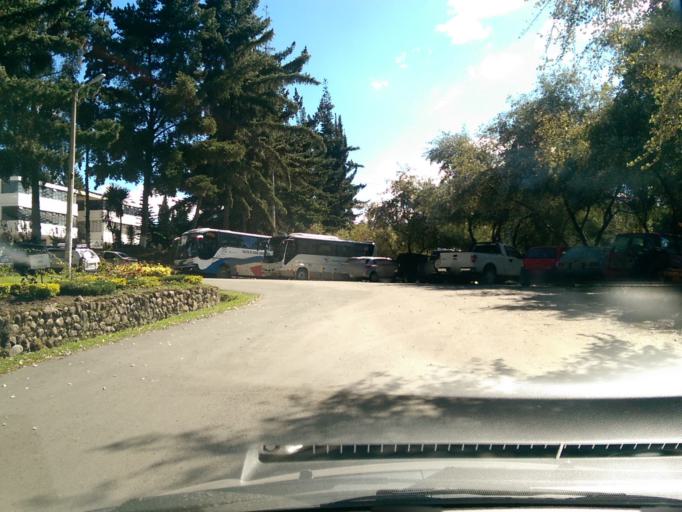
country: EC
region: Azuay
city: Cuenca
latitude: -2.9196
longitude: -79.0246
